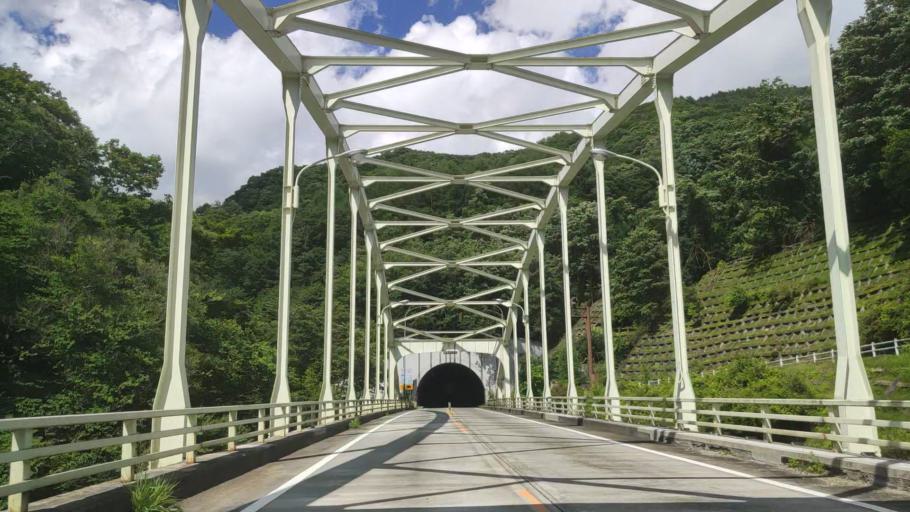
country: JP
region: Yamanashi
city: Enzan
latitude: 35.8640
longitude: 138.7654
